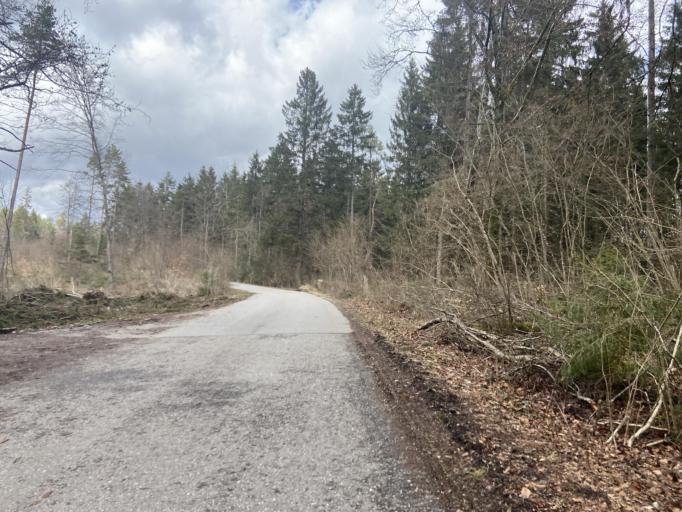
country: DE
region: Baden-Wuerttemberg
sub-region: Tuebingen Region
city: Bingen
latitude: 48.1406
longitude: 9.2419
